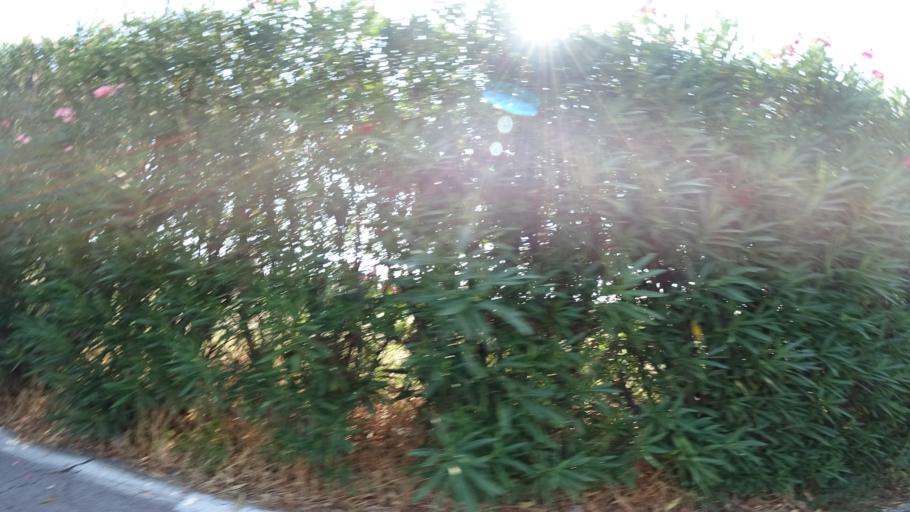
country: FR
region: Languedoc-Roussillon
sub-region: Departement des Pyrenees-Orientales
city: Bompas
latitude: 42.7191
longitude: 2.9324
